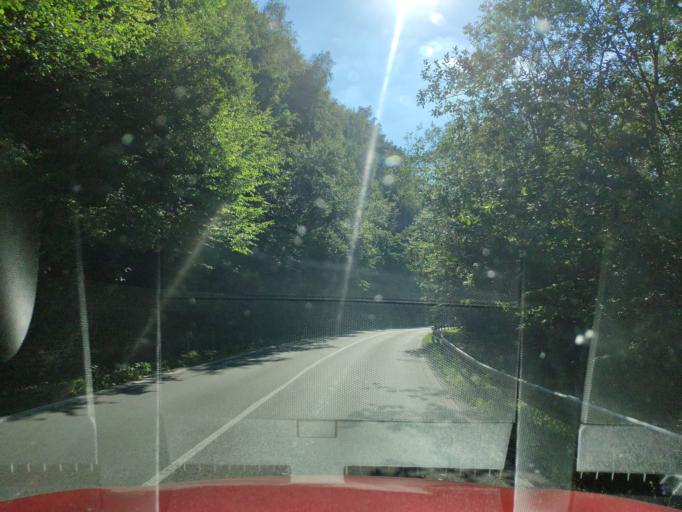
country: SK
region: Presovsky
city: Snina
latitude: 49.0377
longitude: 22.2593
